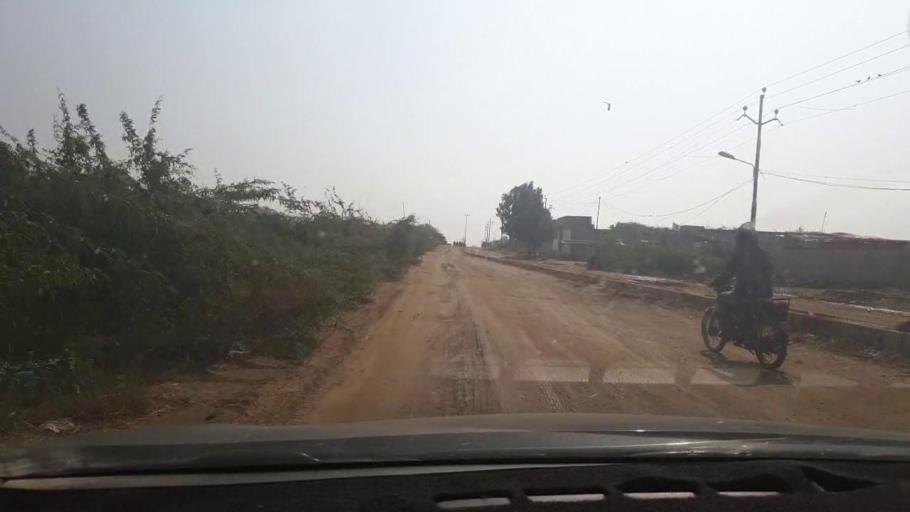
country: PK
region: Sindh
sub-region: Karachi District
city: Karachi
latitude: 25.0022
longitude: 66.9712
